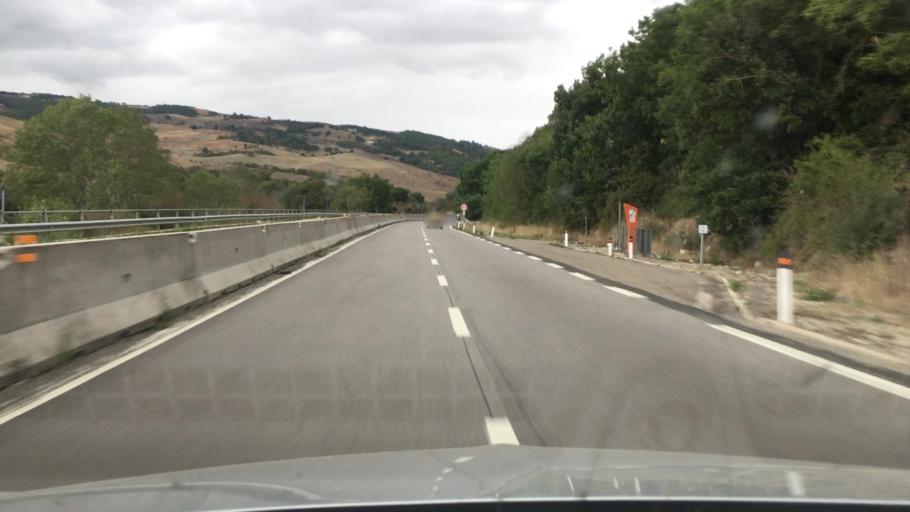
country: IT
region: Basilicate
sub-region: Provincia di Potenza
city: Vaglio Basilicata
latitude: 40.6519
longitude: 15.9165
